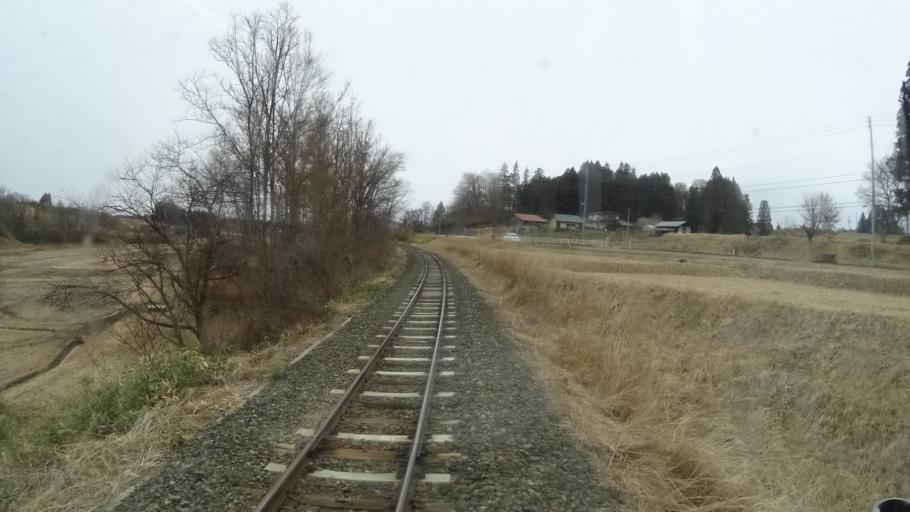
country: JP
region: Iwate
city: Hanamaki
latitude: 39.3975
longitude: 141.2107
